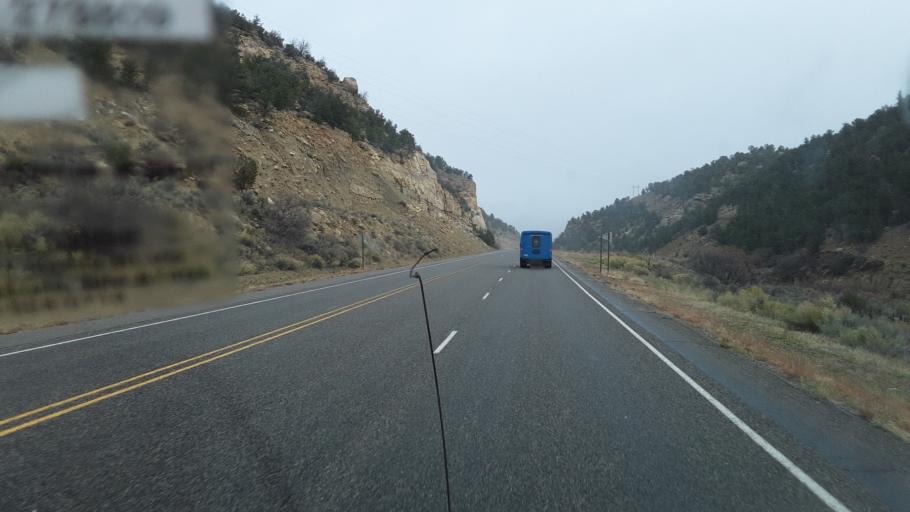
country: US
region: New Mexico
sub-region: Rio Arriba County
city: Tierra Amarilla
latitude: 36.4167
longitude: -106.4815
